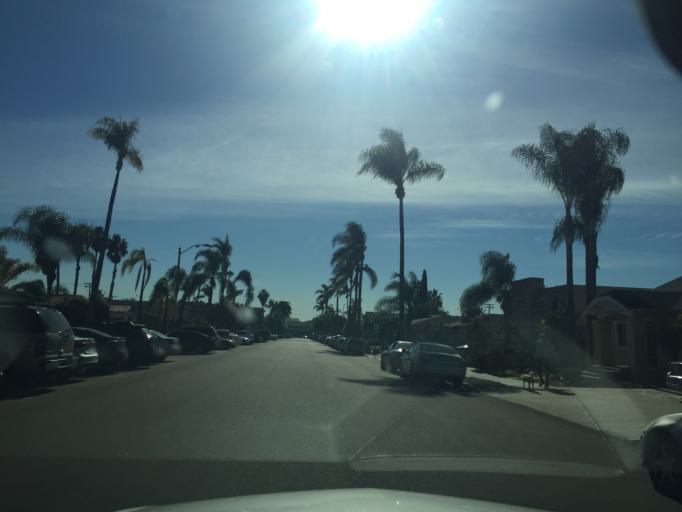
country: US
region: California
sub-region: San Diego County
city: San Diego
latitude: 32.7517
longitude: -117.1277
